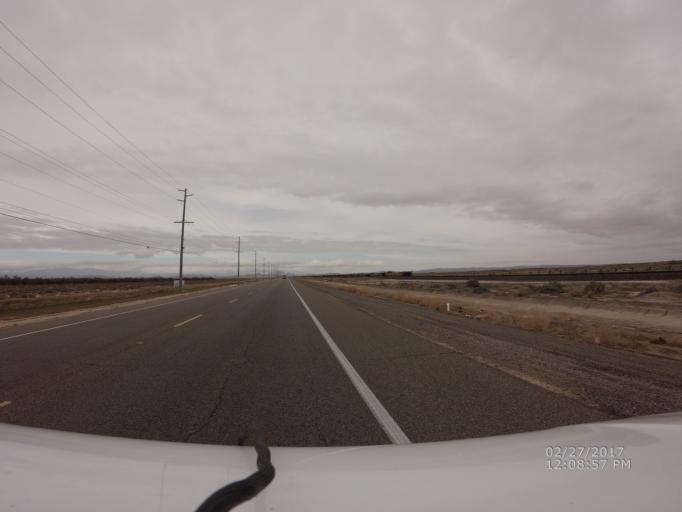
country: US
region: California
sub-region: Los Angeles County
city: Lancaster
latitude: 34.7664
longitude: -118.1475
